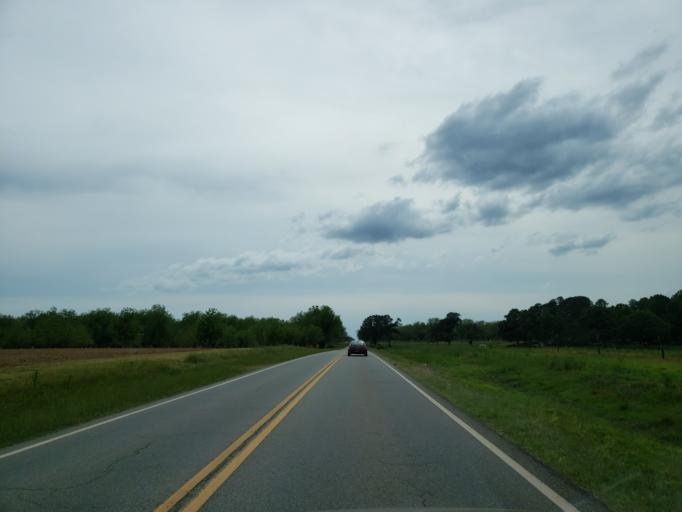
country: US
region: Georgia
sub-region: Houston County
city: Perry
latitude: 32.4387
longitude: -83.7927
